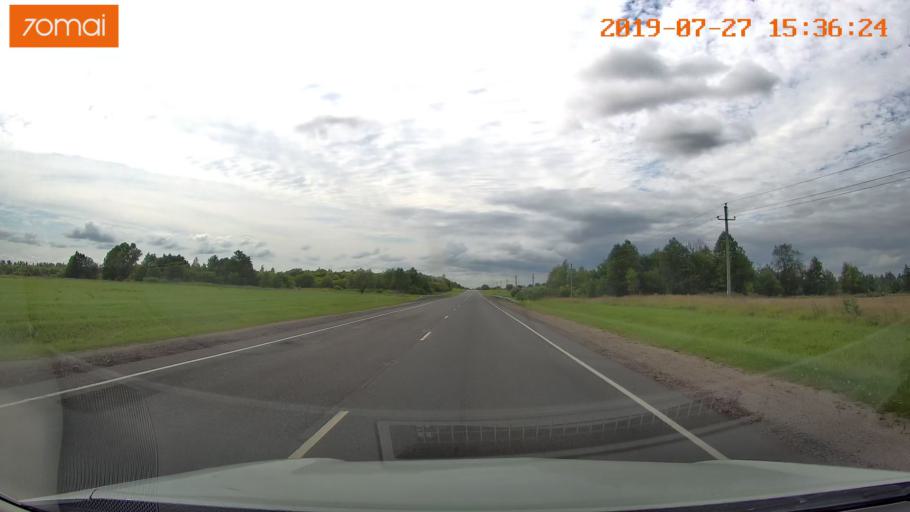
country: RU
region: Kaliningrad
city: Gusev
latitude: 54.6119
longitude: 22.3703
